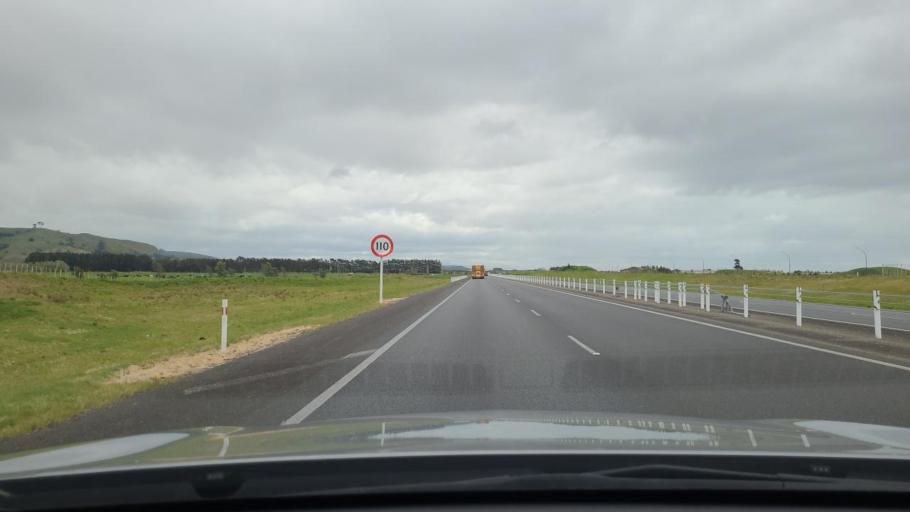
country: NZ
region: Bay of Plenty
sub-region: Western Bay of Plenty District
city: Maketu
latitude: -37.7272
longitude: 176.3286
